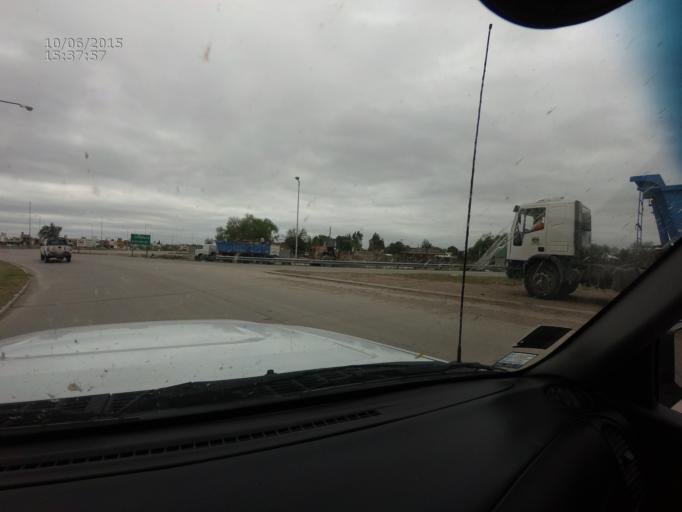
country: AR
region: Cordoba
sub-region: Departamento de Capital
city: Cordoba
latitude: -31.3536
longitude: -64.2264
